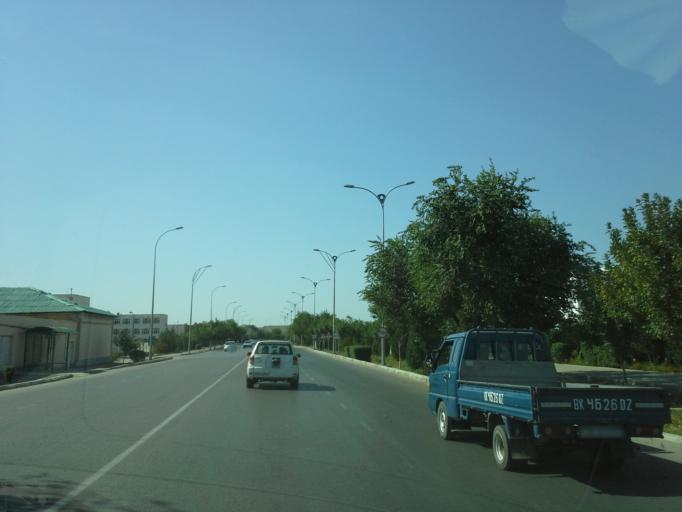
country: TM
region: Dasoguz
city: Dasoguz
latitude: 41.8402
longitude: 59.9445
